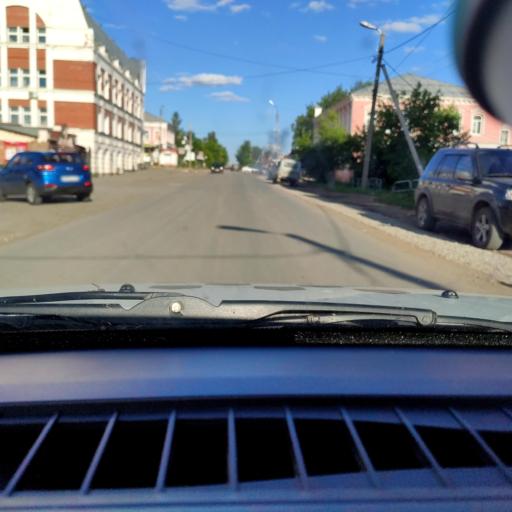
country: RU
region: Perm
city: Ocher
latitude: 57.8855
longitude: 54.7144
